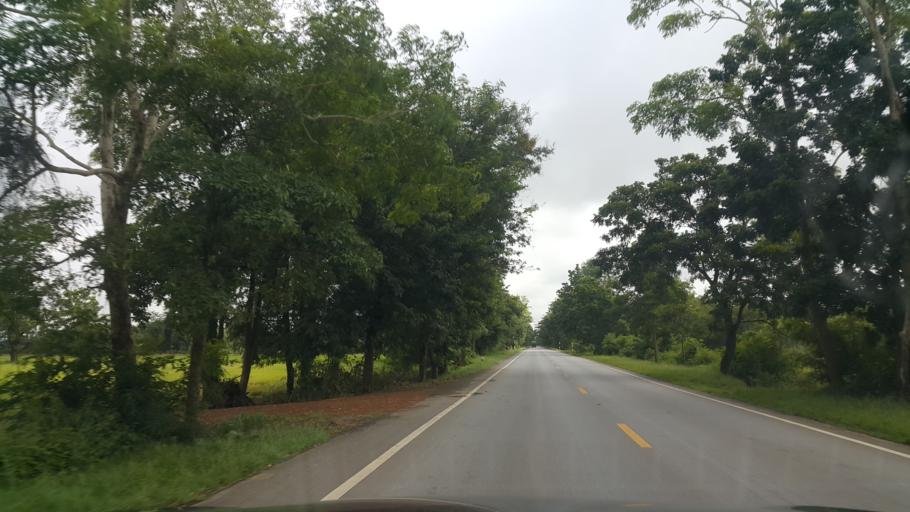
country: TH
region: Sukhothai
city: Sawankhalok
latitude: 17.3310
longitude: 99.7397
